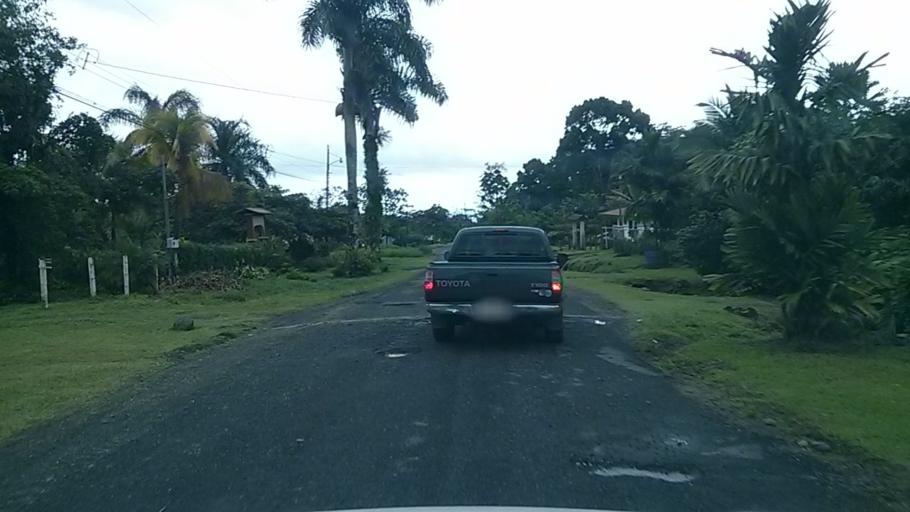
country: CR
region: Limon
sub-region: Canton de Pococi
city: Guapiles
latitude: 10.1740
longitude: -83.7837
